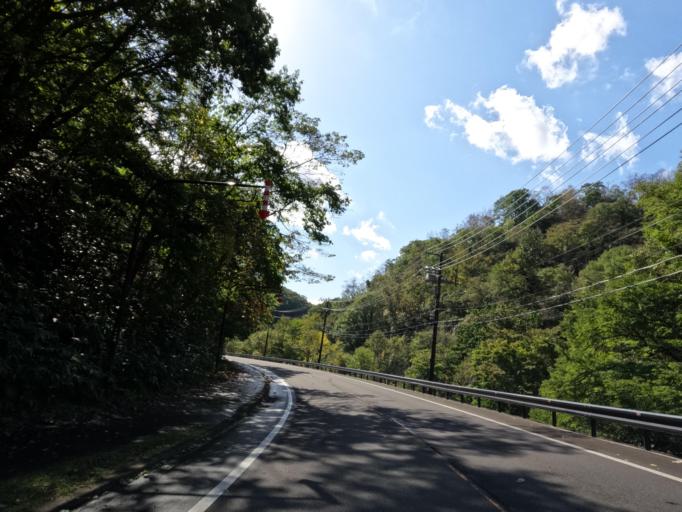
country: JP
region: Hokkaido
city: Shiraoi
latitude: 42.4850
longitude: 141.1448
